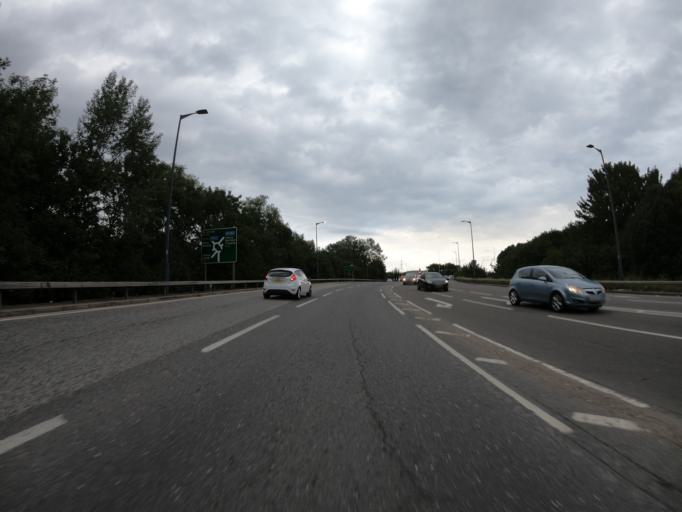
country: GB
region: England
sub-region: Greater London
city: Barking
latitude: 51.5232
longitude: 0.0724
